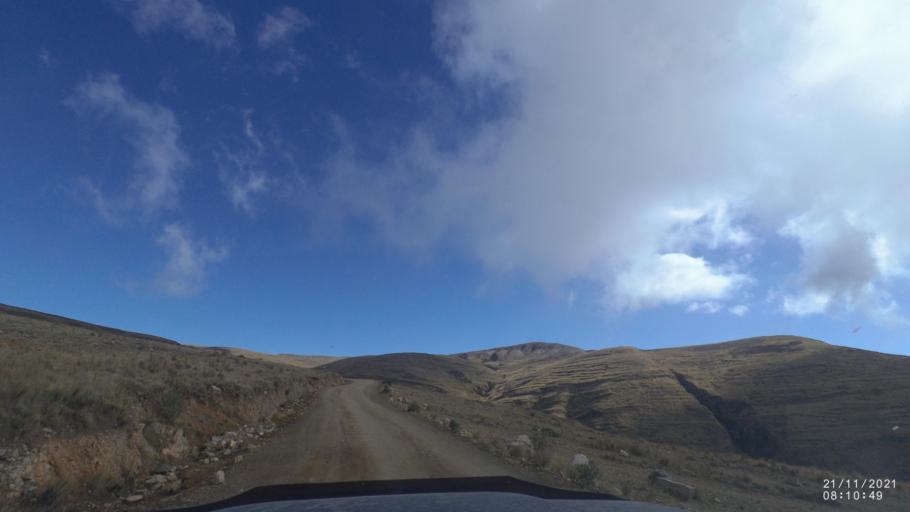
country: BO
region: Cochabamba
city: Cochabamba
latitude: -17.2829
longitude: -66.2102
